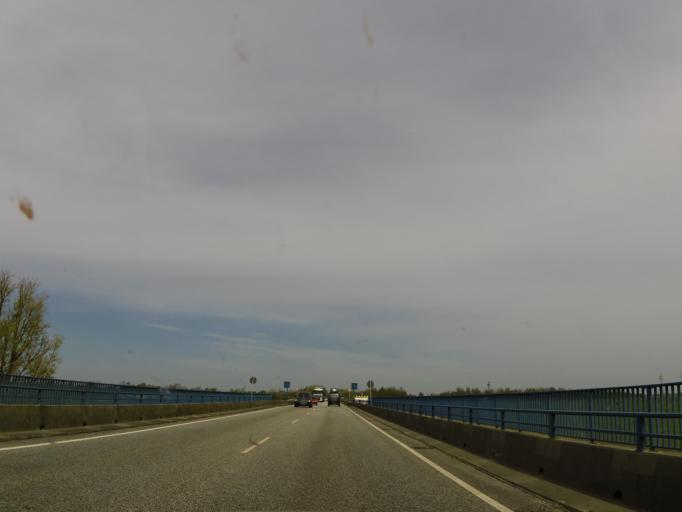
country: DE
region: Schleswig-Holstein
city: Tonning
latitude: 54.3160
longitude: 8.9566
